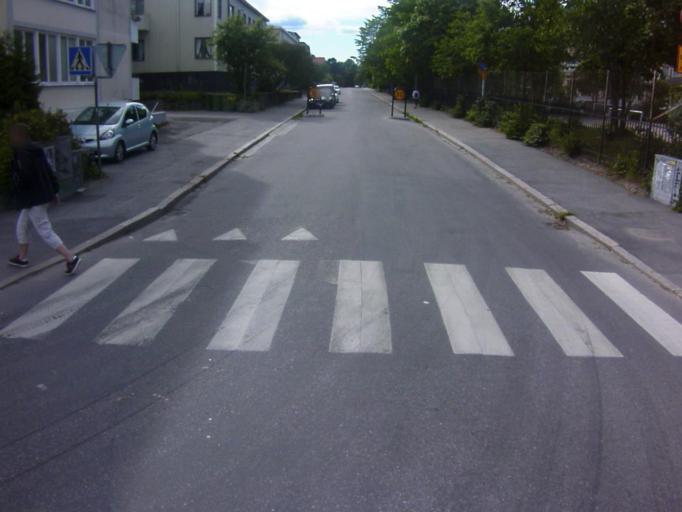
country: SE
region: Soedermanland
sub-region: Eskilstuna Kommun
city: Eskilstuna
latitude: 59.3643
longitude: 16.5079
